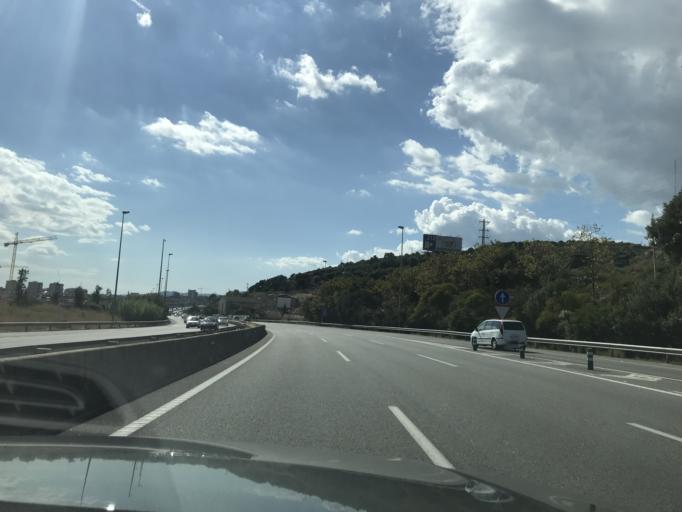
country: ES
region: Catalonia
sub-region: Provincia de Barcelona
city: Montgat
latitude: 41.4653
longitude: 2.2727
